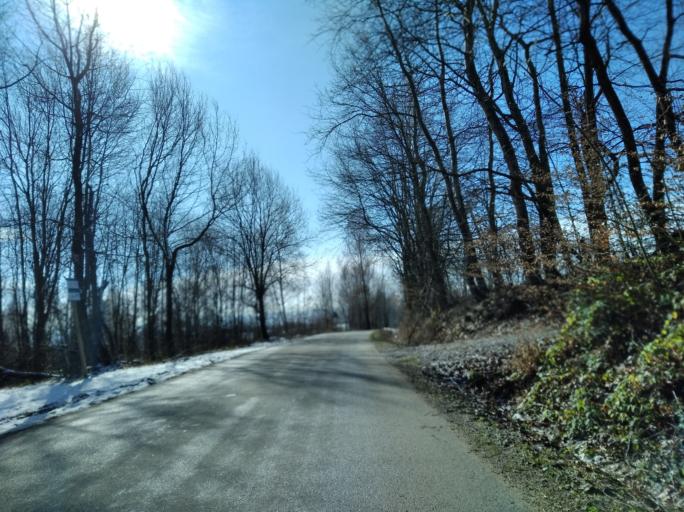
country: PL
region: Subcarpathian Voivodeship
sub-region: Powiat brzozowski
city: Jablonica Polska
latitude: 49.7199
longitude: 21.8827
